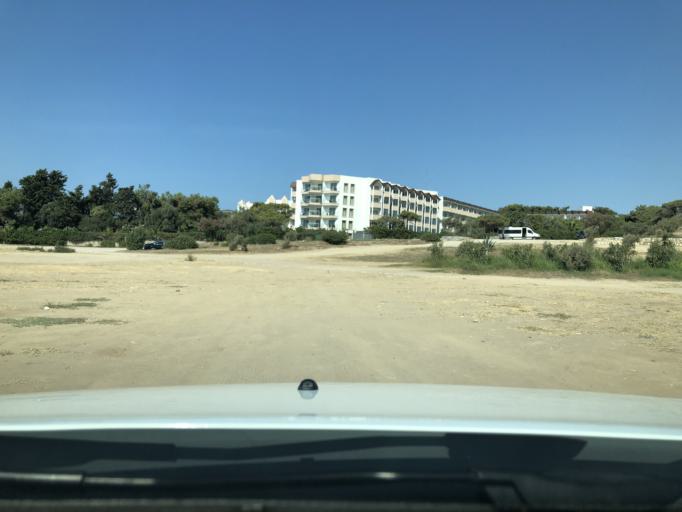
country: TR
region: Antalya
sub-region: Manavgat
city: Manavgat
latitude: 36.7569
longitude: 31.4241
